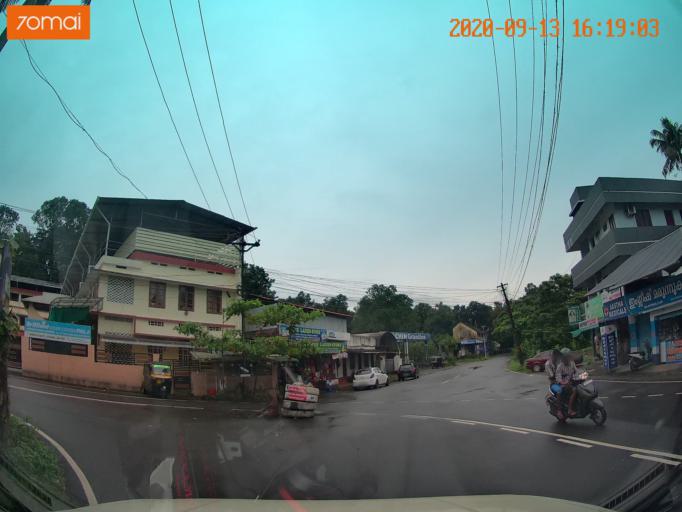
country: IN
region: Kerala
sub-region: Kottayam
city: Lalam
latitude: 9.7044
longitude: 76.6626
